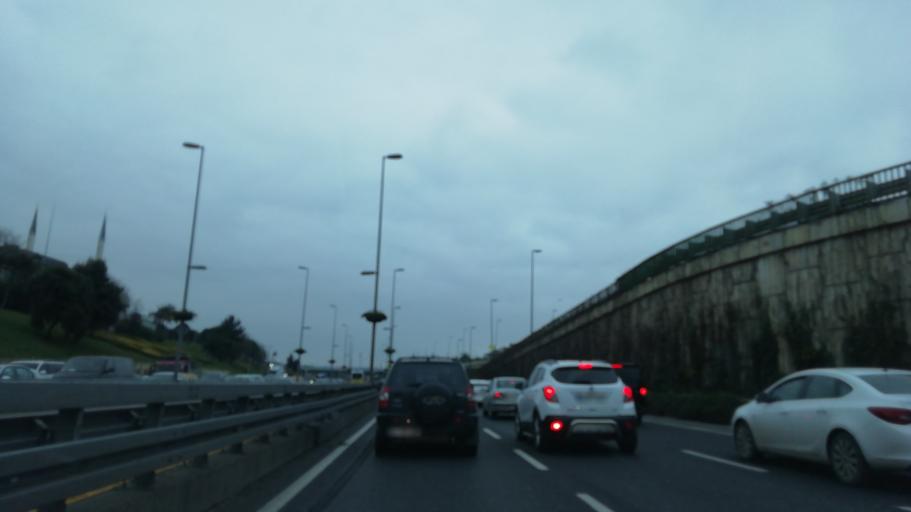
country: TR
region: Istanbul
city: UEskuedar
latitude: 41.0266
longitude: 29.0461
